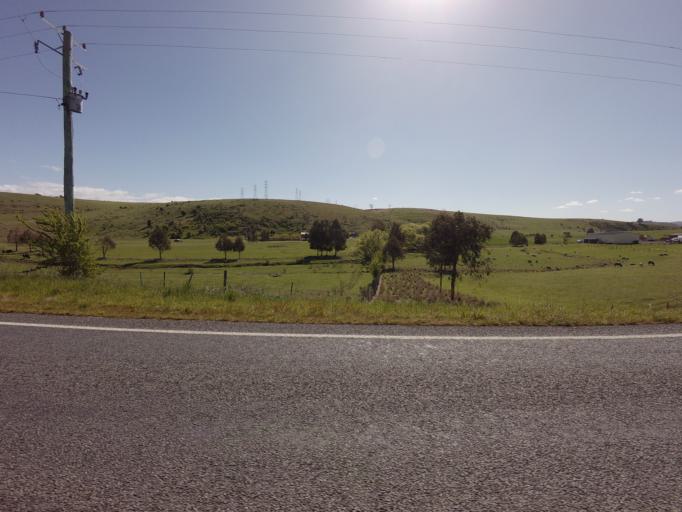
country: AU
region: Tasmania
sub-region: Derwent Valley
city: New Norfolk
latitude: -42.6616
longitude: 146.9346
